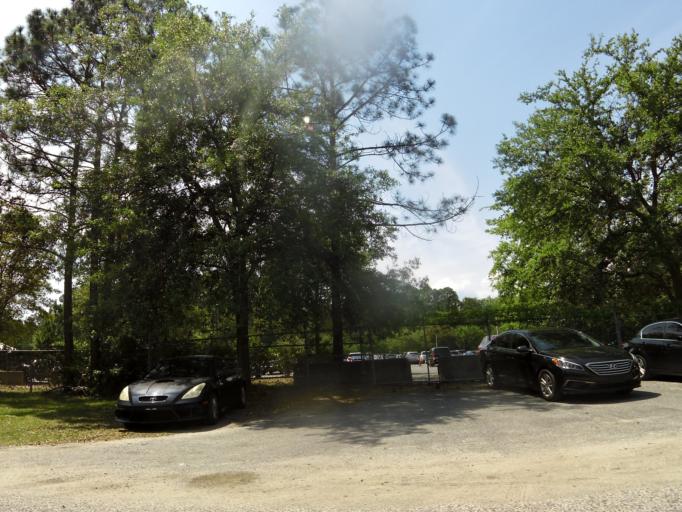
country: US
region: Florida
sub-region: Nassau County
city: Nassau Village-Ratliff
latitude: 30.4920
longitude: -81.6676
